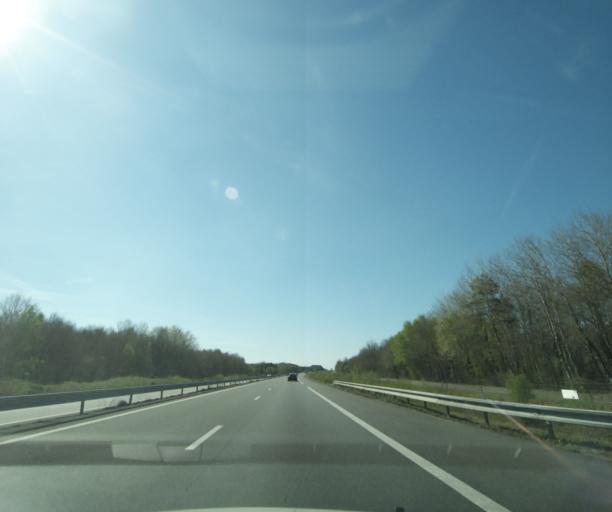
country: FR
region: Centre
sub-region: Departement du Loir-et-Cher
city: Salbris
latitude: 47.3702
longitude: 2.0537
